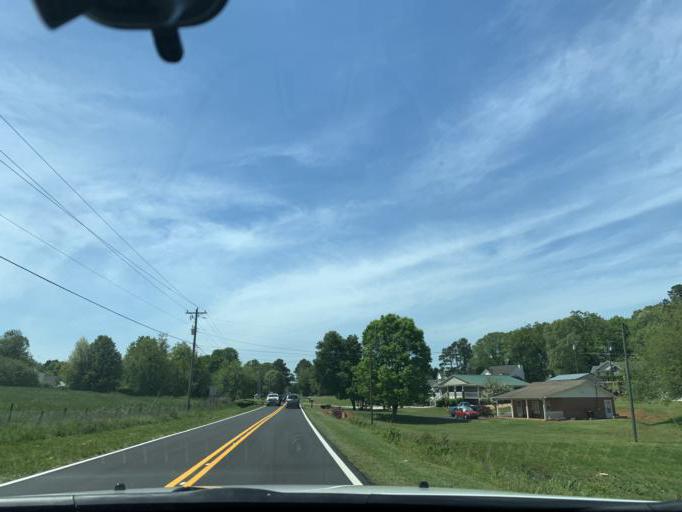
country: US
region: Georgia
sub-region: Forsyth County
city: Cumming
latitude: 34.2601
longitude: -84.0299
